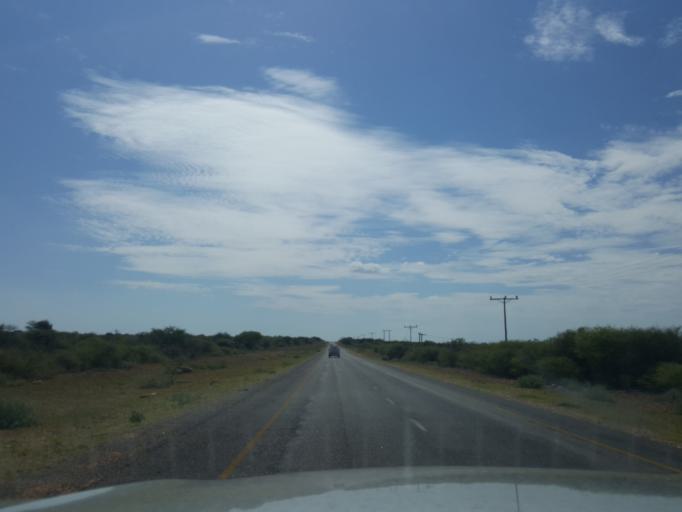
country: BW
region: Kweneng
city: Letlhakeng
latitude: -24.1534
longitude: 25.1591
